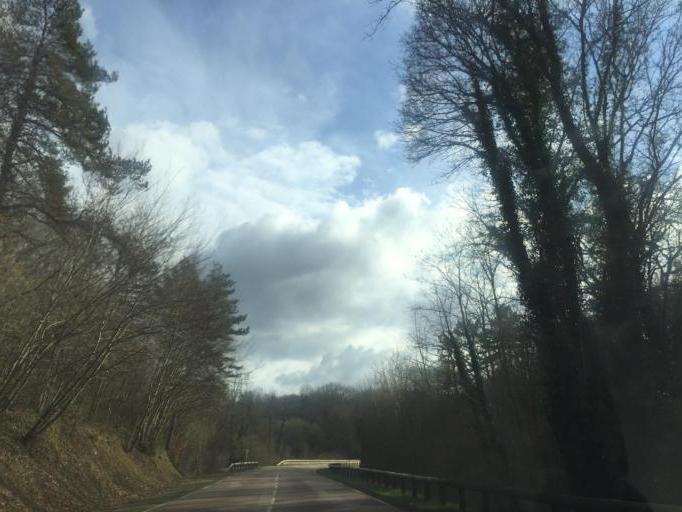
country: FR
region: Bourgogne
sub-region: Departement de l'Yonne
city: Avallon
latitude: 47.4577
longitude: 3.7153
